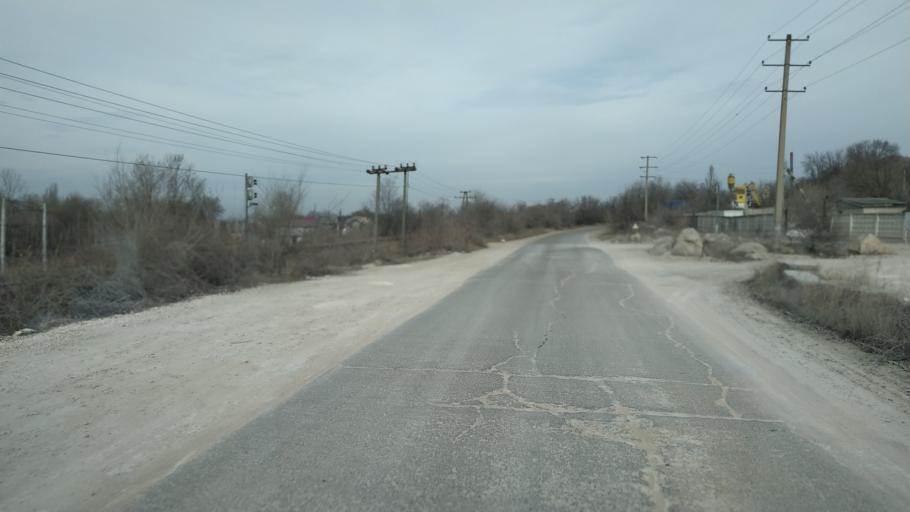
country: MD
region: Chisinau
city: Vatra
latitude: 47.0771
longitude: 28.7425
